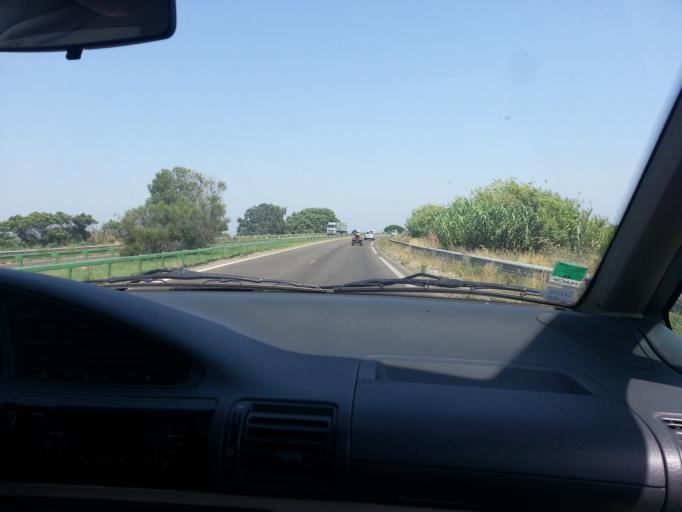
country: FR
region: Languedoc-Roussillon
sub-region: Departement de l'Herault
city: Perols
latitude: 43.5509
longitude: 3.9749
